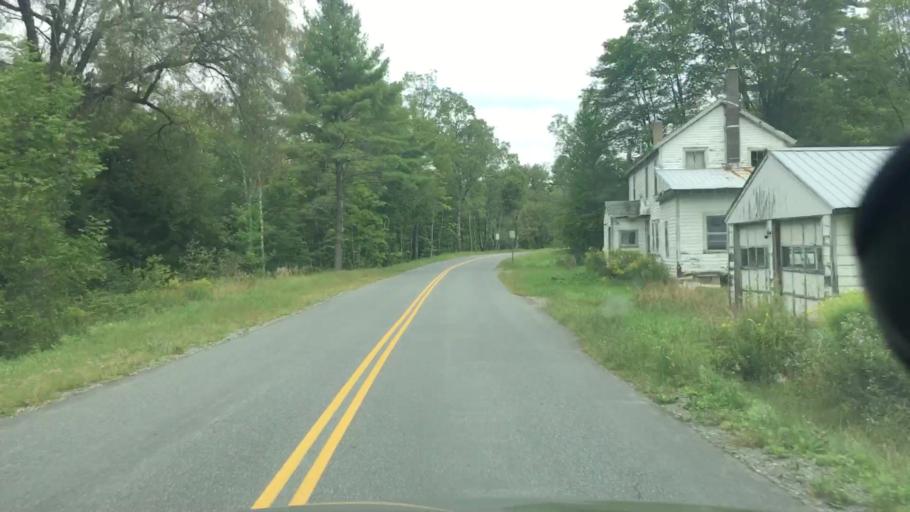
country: US
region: Massachusetts
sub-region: Franklin County
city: Colrain
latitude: 42.7806
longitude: -72.7689
